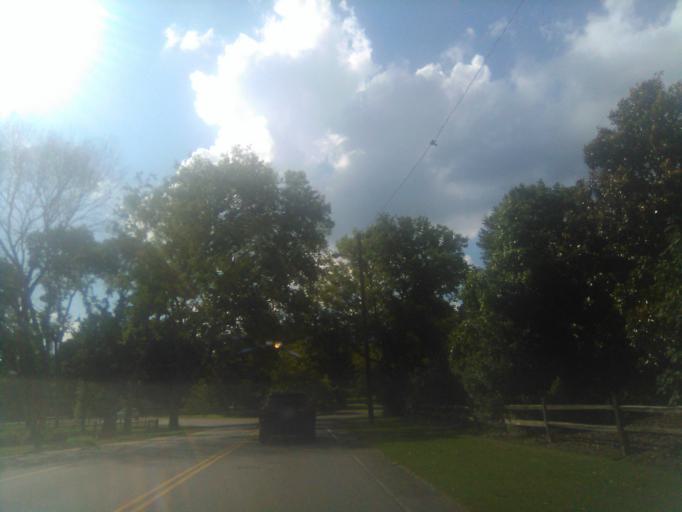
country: US
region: Tennessee
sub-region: Davidson County
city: Belle Meade
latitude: 36.0963
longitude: -86.8604
